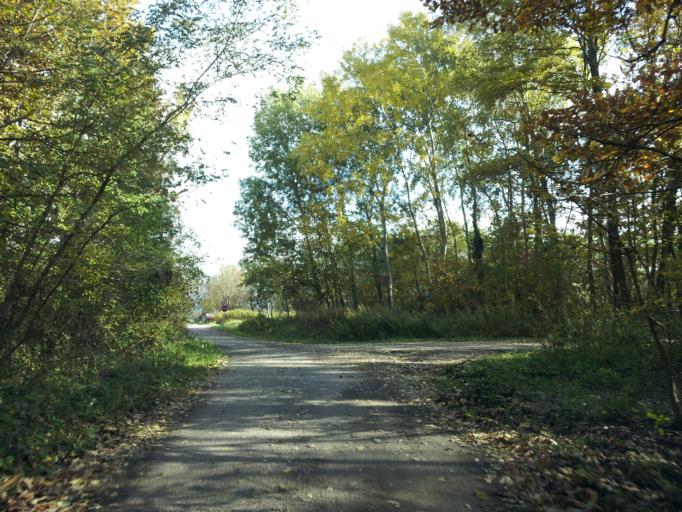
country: HU
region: Gyor-Moson-Sopron
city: Bakonyszentlaszlo
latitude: 47.3665
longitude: 17.8176
